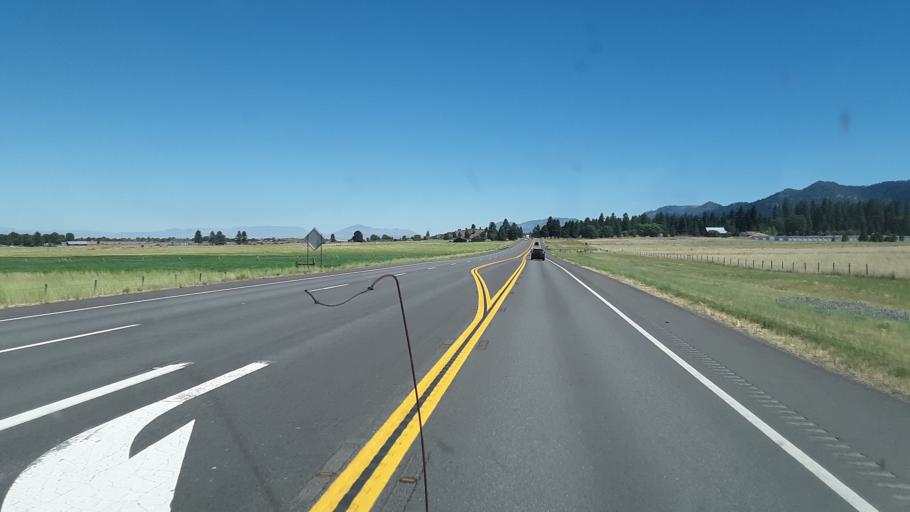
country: US
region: California
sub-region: Lassen County
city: Janesville
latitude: 40.3132
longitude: -120.5374
